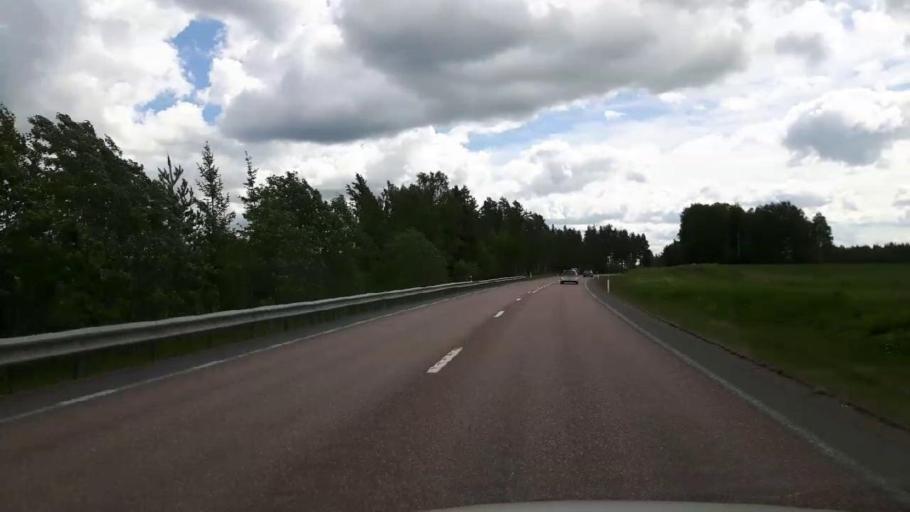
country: SE
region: Dalarna
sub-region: Saters Kommun
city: Saeter
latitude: 60.4720
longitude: 15.7939
